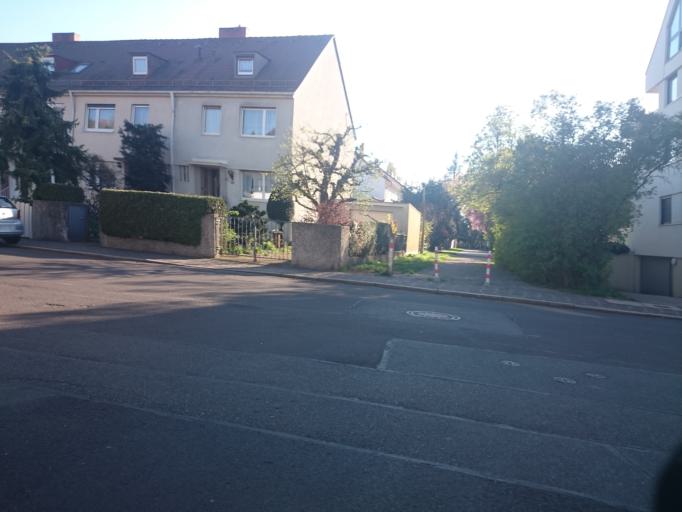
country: DE
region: Bavaria
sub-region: Regierungsbezirk Mittelfranken
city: Nuernberg
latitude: 49.4549
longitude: 11.1277
